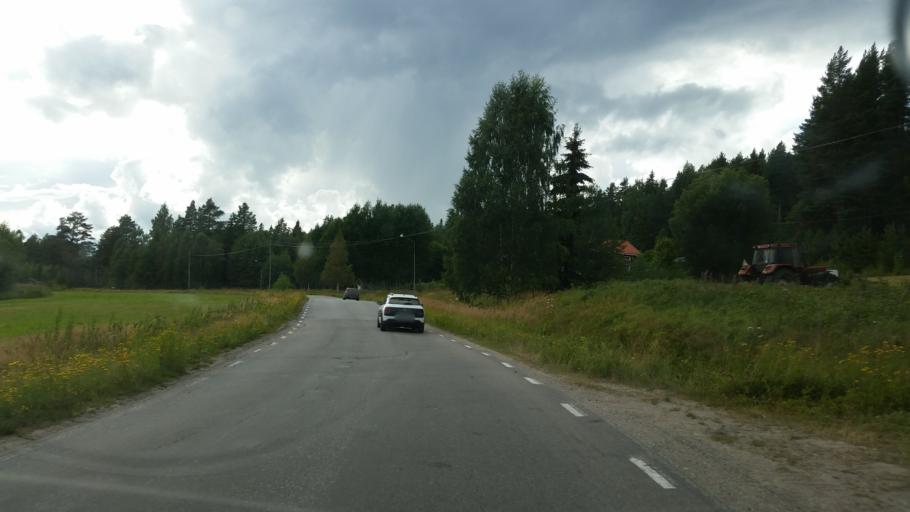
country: SE
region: Gaevleborg
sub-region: Hudiksvalls Kommun
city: Delsbo
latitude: 61.9193
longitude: 16.6042
